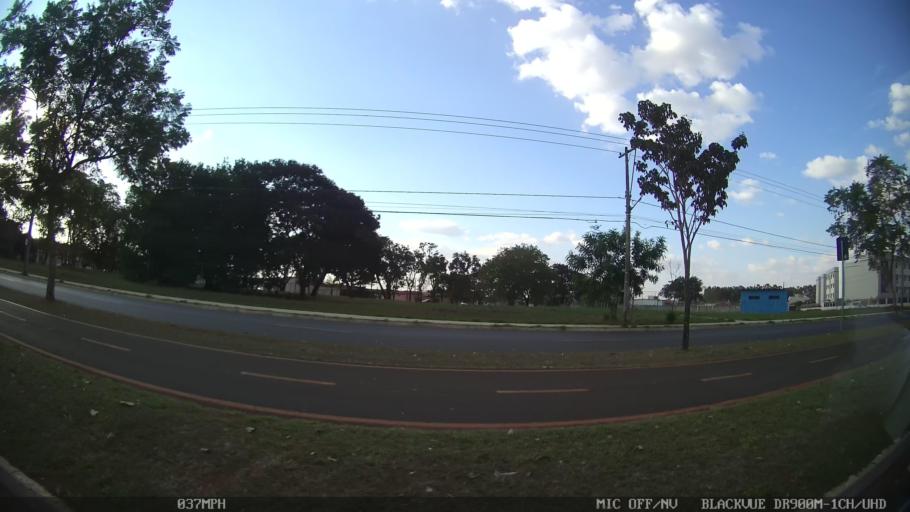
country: BR
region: Sao Paulo
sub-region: Ribeirao Preto
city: Ribeirao Preto
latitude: -21.1936
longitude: -47.7405
